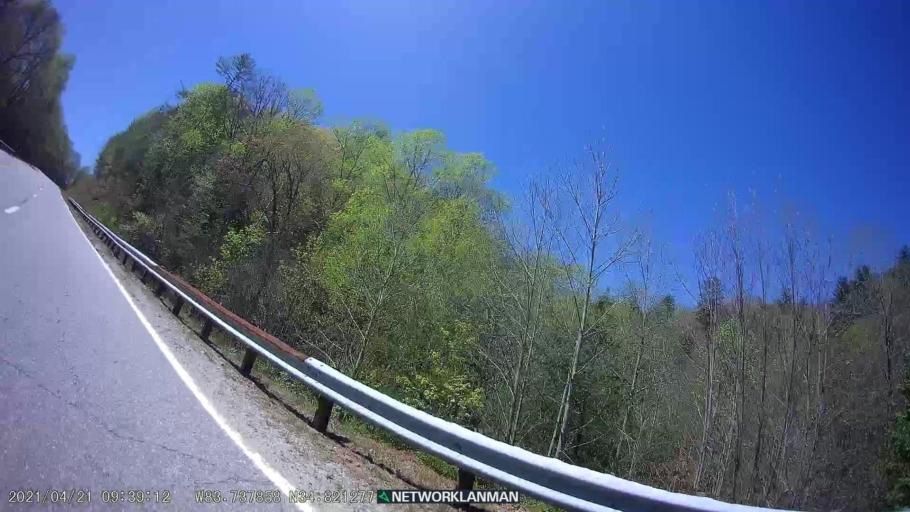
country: US
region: Georgia
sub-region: Towns County
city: Hiawassee
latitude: 34.8212
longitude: -83.7379
